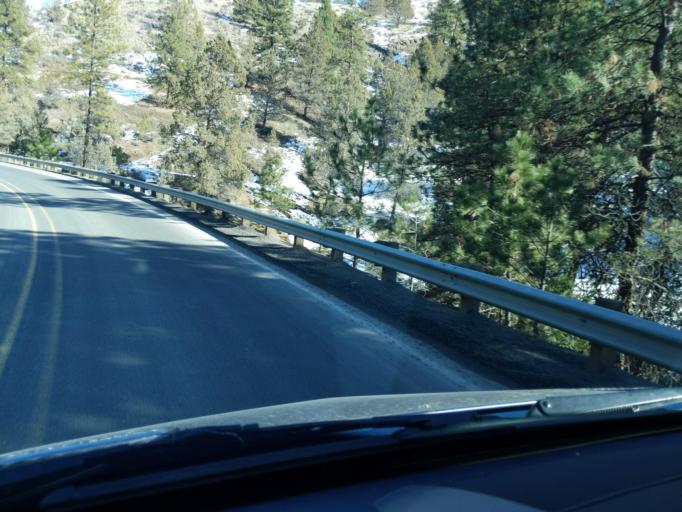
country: US
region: Oregon
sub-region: Grant County
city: John Day
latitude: 44.8351
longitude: -119.0401
